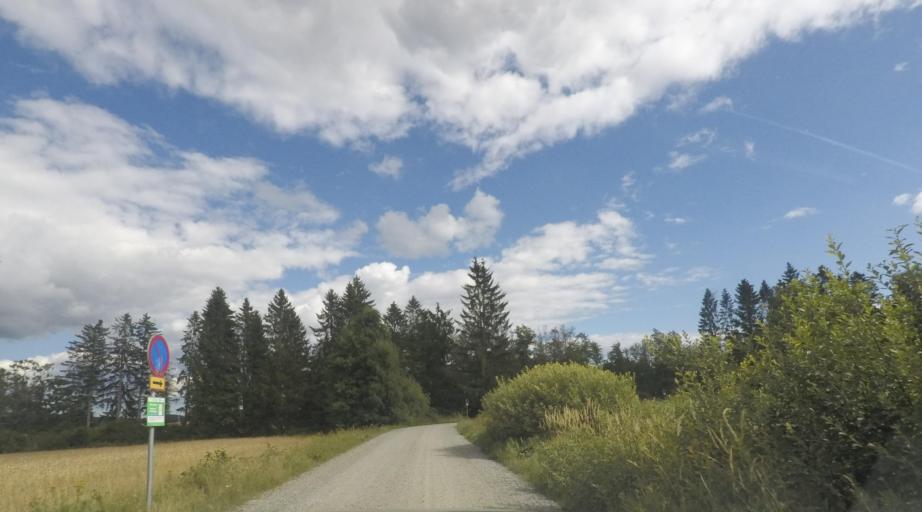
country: SE
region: Stockholm
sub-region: Sodertalje Kommun
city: Pershagen
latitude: 59.1066
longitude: 17.6778
